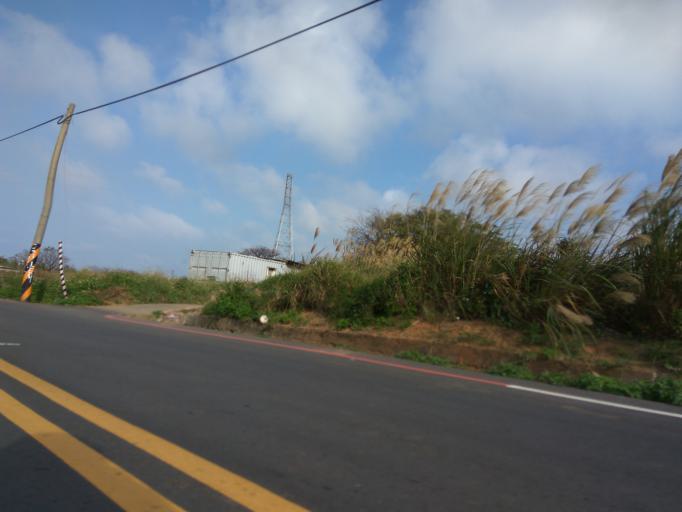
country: TW
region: Taiwan
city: Taoyuan City
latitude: 25.0661
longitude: 121.1725
